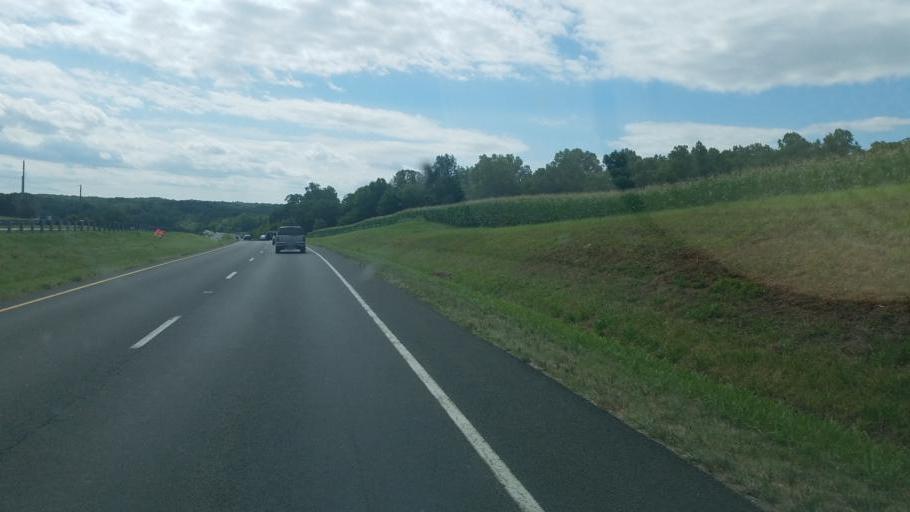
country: US
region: Virginia
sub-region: Fauquier County
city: Bealeton
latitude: 38.4371
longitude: -77.6400
